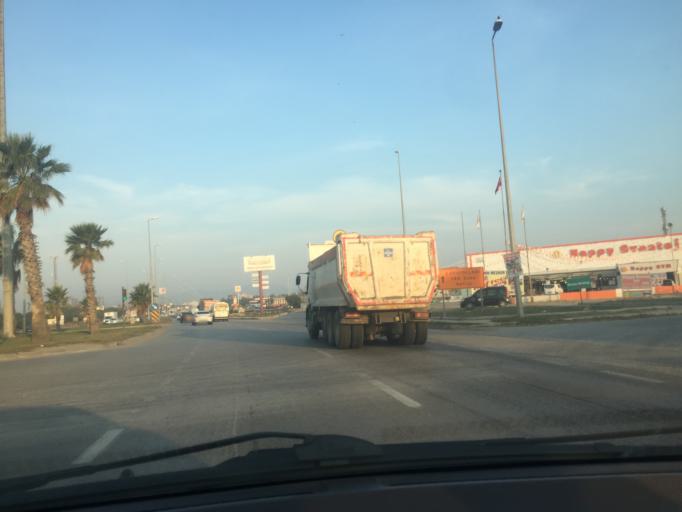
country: TR
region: Balikesir
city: Bandirma
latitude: 40.3239
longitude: 28.0041
